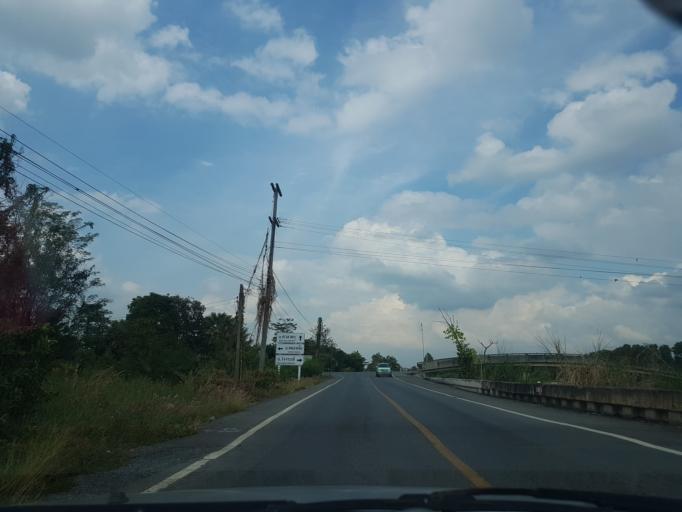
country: TH
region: Pathum Thani
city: Nong Suea
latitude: 14.1958
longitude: 100.8915
